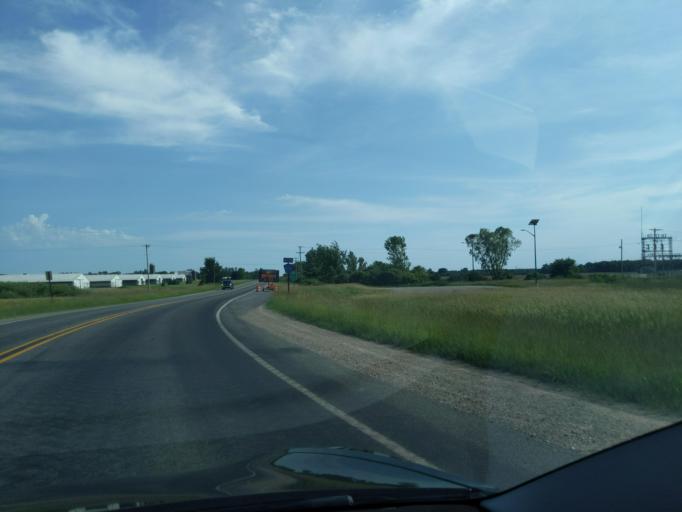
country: US
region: Michigan
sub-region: Newaygo County
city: Fremont
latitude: 43.4253
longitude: -86.0393
